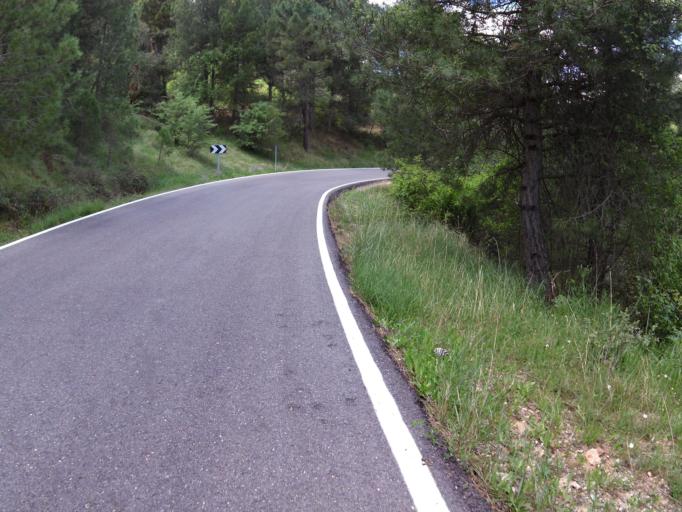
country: ES
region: Castille-La Mancha
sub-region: Provincia de Albacete
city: Paterna del Madera
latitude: 38.5696
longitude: -2.3830
